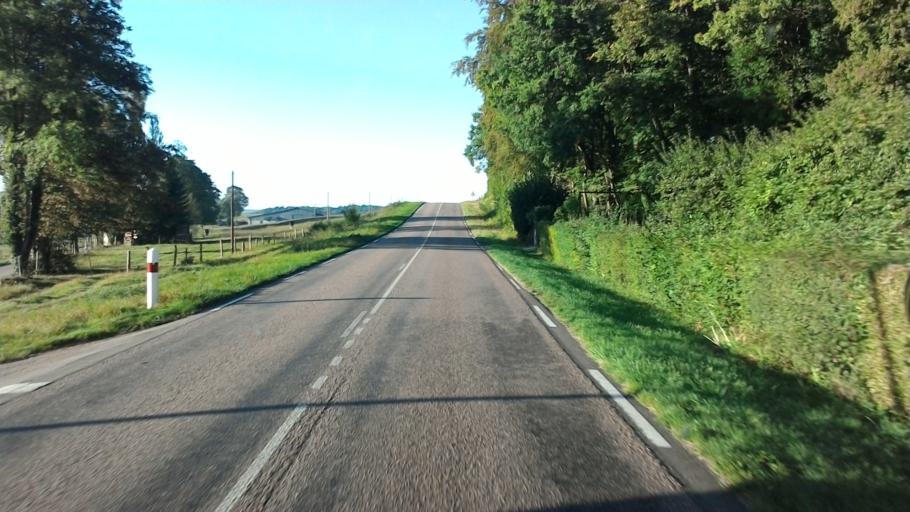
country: FR
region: Lorraine
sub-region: Departement des Vosges
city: Neufchateau
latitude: 48.2996
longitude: 5.6551
